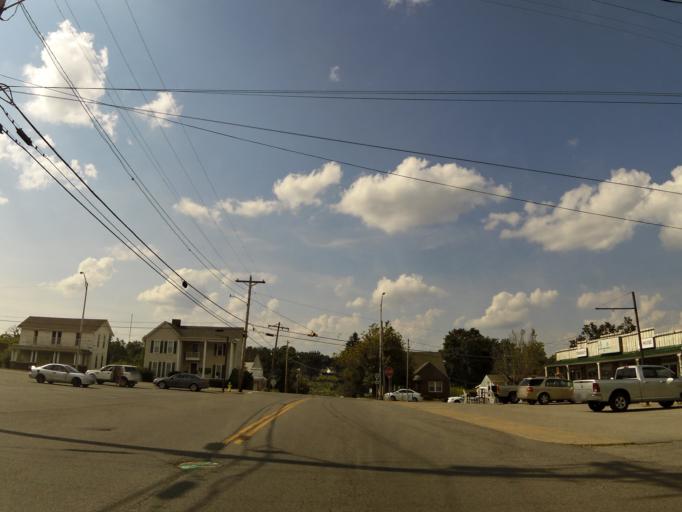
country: US
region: Tennessee
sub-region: Dickson County
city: Dickson
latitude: 36.0782
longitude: -87.3850
